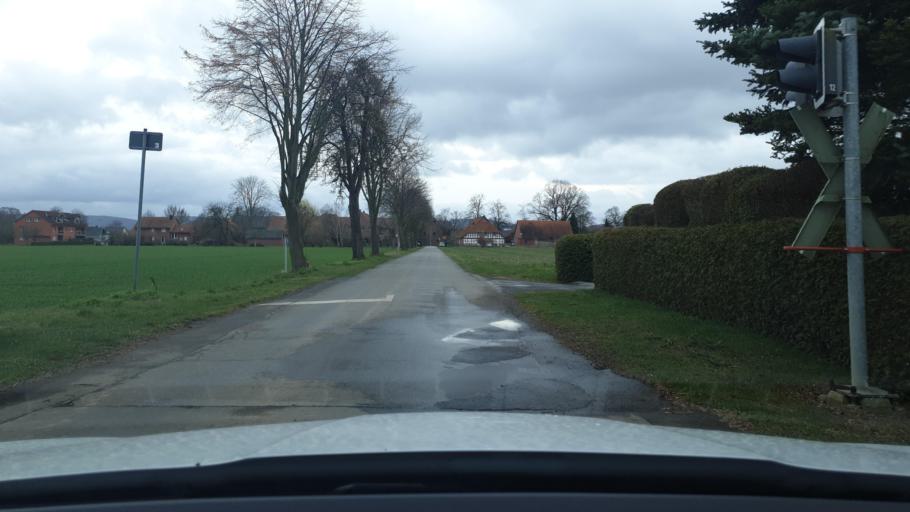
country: DE
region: North Rhine-Westphalia
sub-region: Regierungsbezirk Detmold
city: Hille
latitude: 52.3231
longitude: 8.7954
